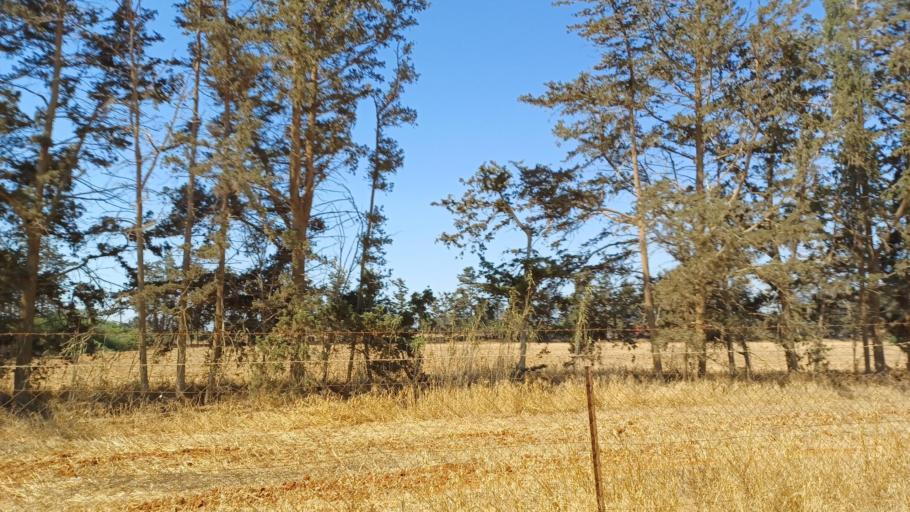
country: CY
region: Ammochostos
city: Avgorou
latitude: 35.0092
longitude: 33.8143
